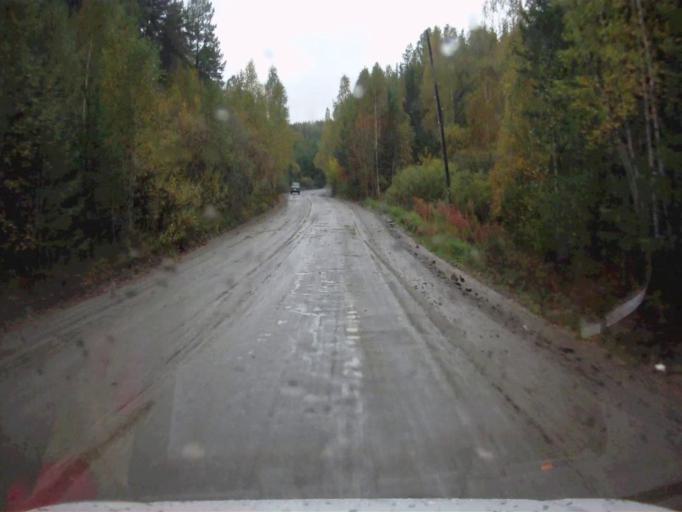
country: RU
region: Chelyabinsk
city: Kyshtym
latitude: 55.7468
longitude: 60.4910
